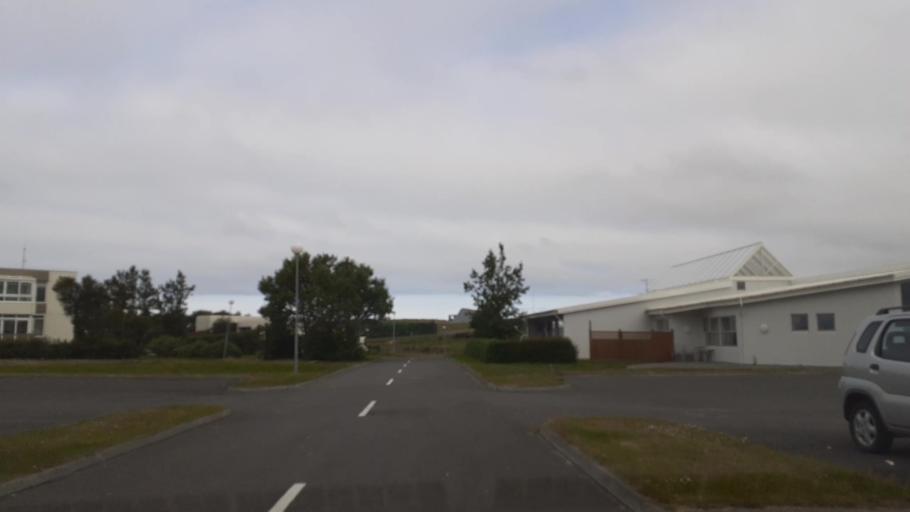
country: IS
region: Northwest
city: Saudarkrokur
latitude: 65.6558
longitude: -20.2779
